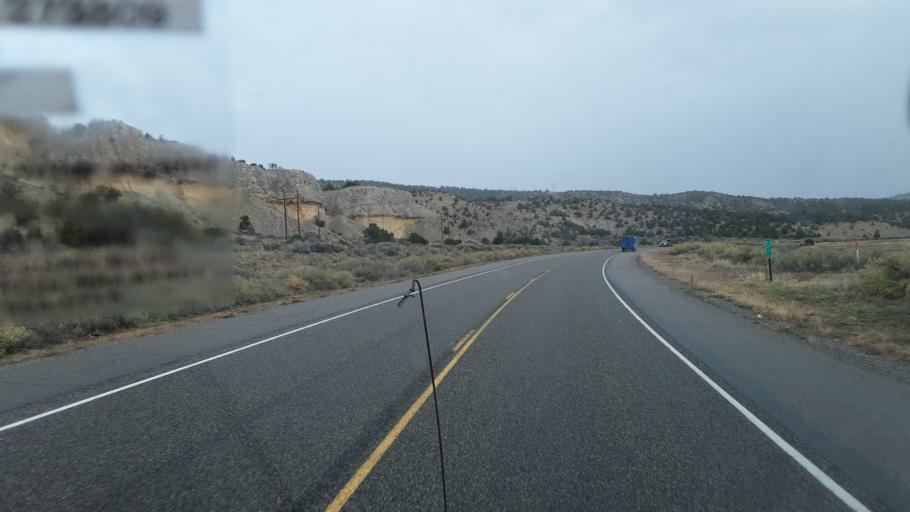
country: US
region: New Mexico
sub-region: Rio Arriba County
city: Santa Teresa
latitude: 36.3819
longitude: -106.5043
